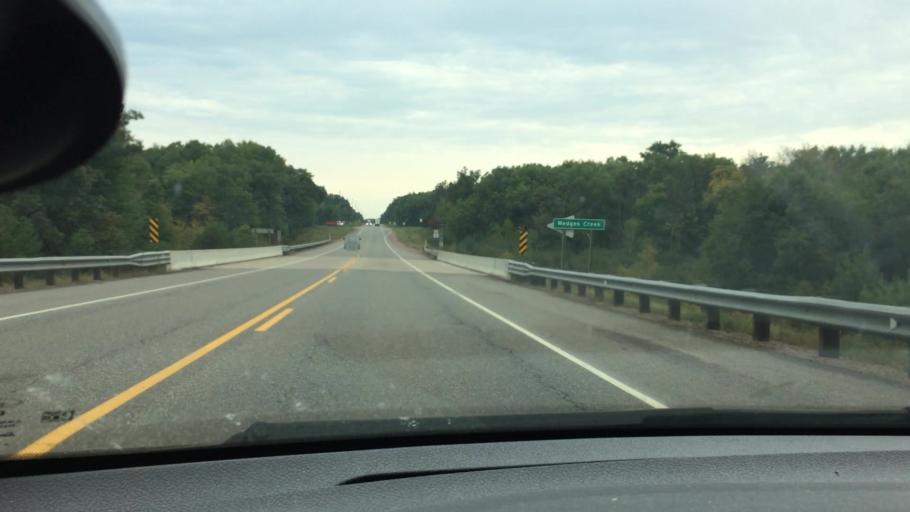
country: US
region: Wisconsin
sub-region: Clark County
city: Neillsville
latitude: 44.5702
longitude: -90.7269
